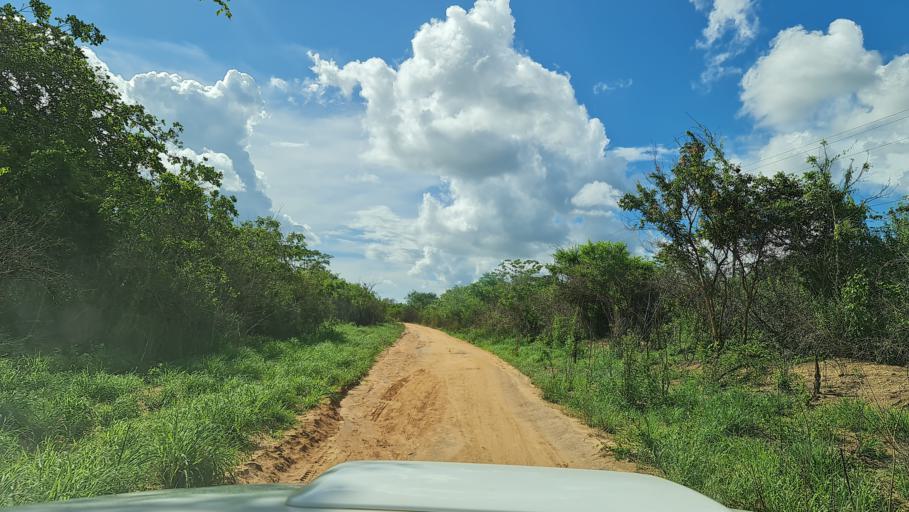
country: MZ
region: Nampula
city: Ilha de Mocambique
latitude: -15.4136
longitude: 40.2557
